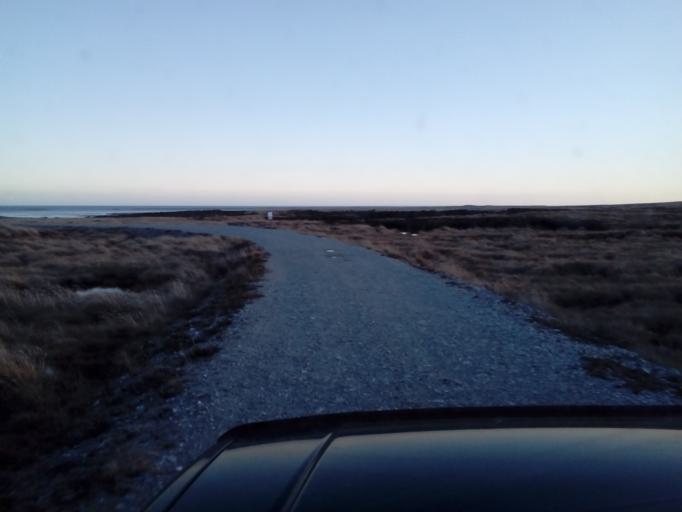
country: FK
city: Stanley
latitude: -51.7034
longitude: -57.8438
